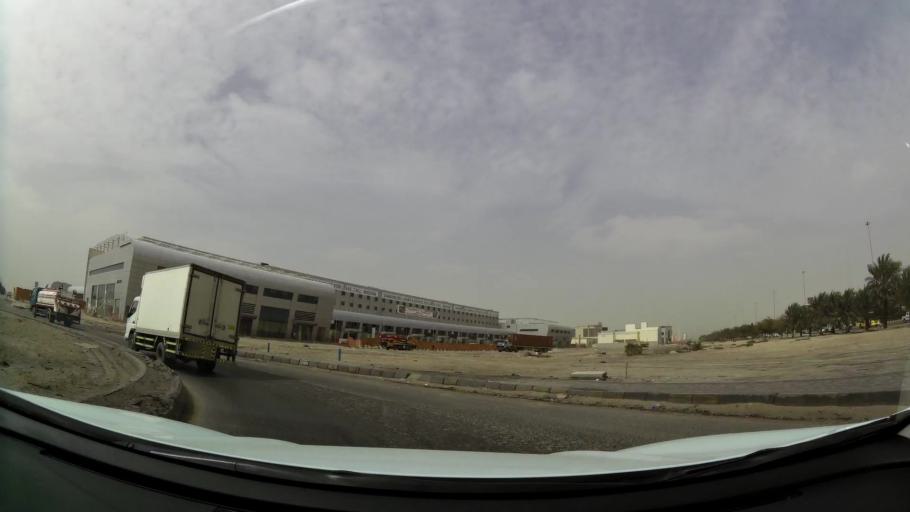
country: AE
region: Abu Dhabi
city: Abu Dhabi
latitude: 24.3559
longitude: 54.5250
